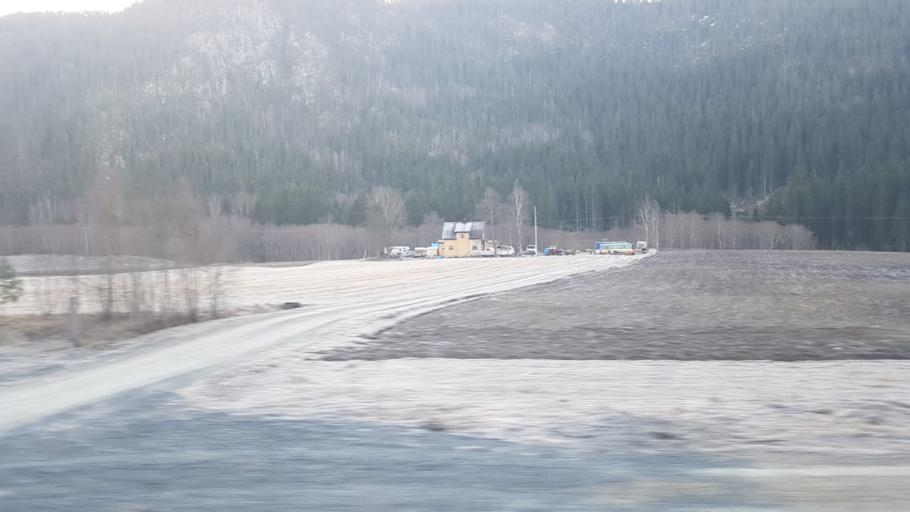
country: NO
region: Nord-Trondelag
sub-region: Stjordal
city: Stjordalshalsen
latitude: 63.5921
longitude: 11.0149
